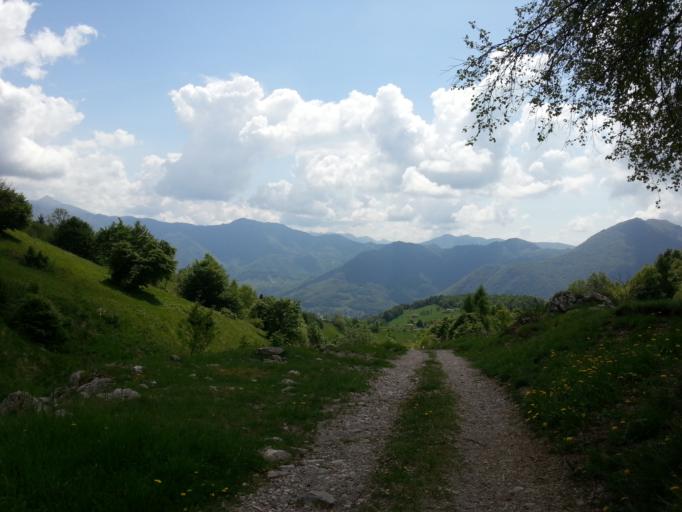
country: IT
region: Lombardy
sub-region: Provincia di Lecco
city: Pasturo
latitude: 45.9460
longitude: 9.4109
